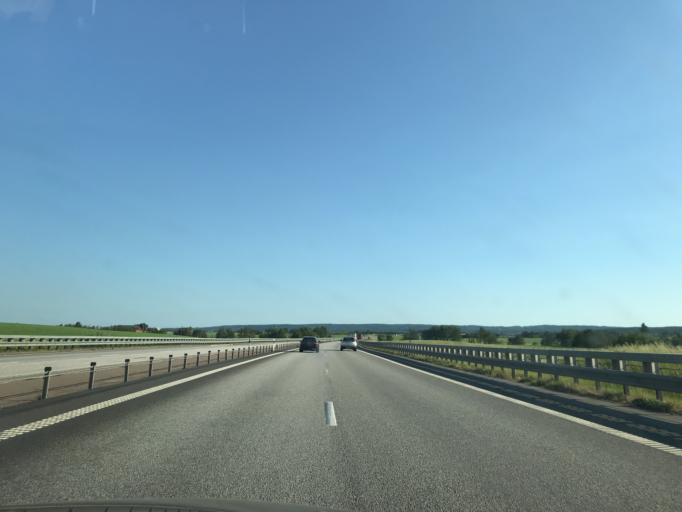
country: SE
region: Skane
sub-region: Angelholms Kommun
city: AEngelholm
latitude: 56.2642
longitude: 12.8943
